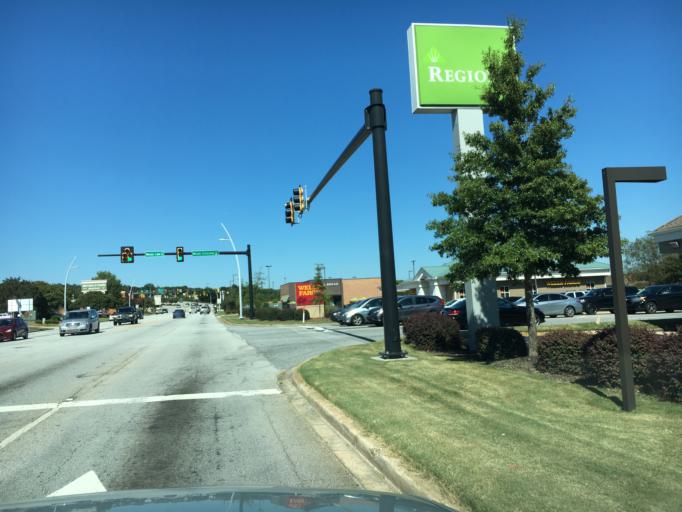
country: US
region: South Carolina
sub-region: Greenville County
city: Wade Hampton
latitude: 34.8494
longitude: -82.3379
